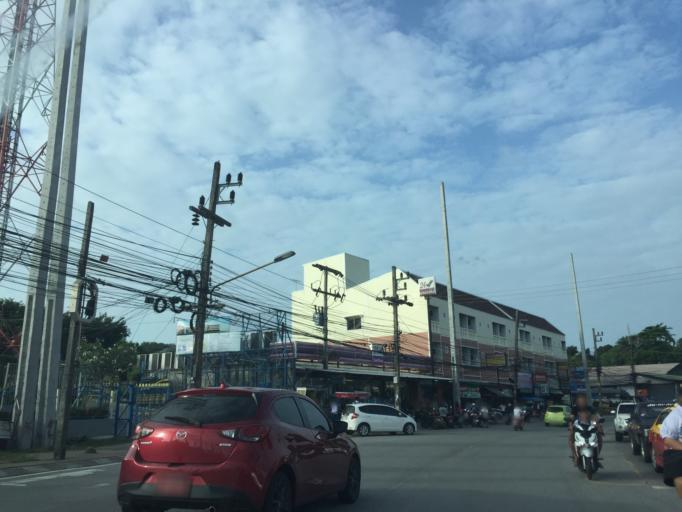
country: TH
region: Phuket
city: Mueang Phuket
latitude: 7.8679
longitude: 98.3740
